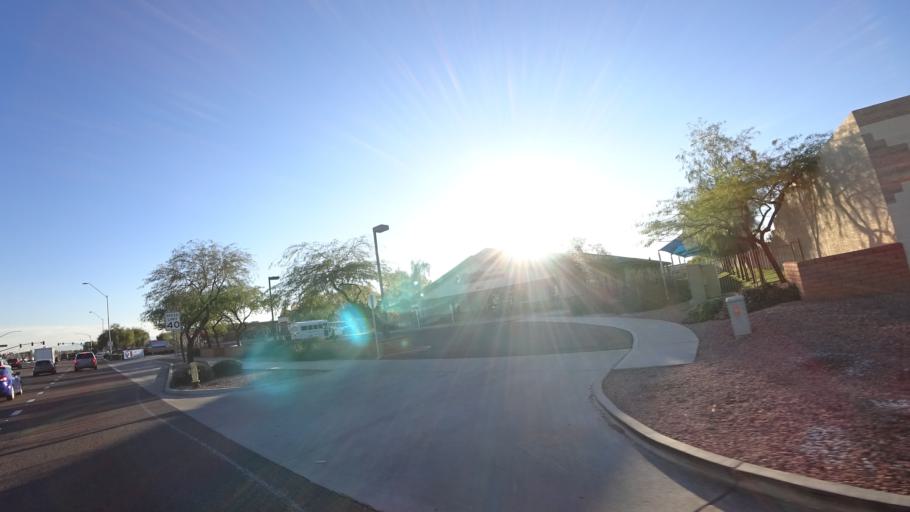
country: US
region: Arizona
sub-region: Maricopa County
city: Sun City
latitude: 33.6546
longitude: -112.2378
